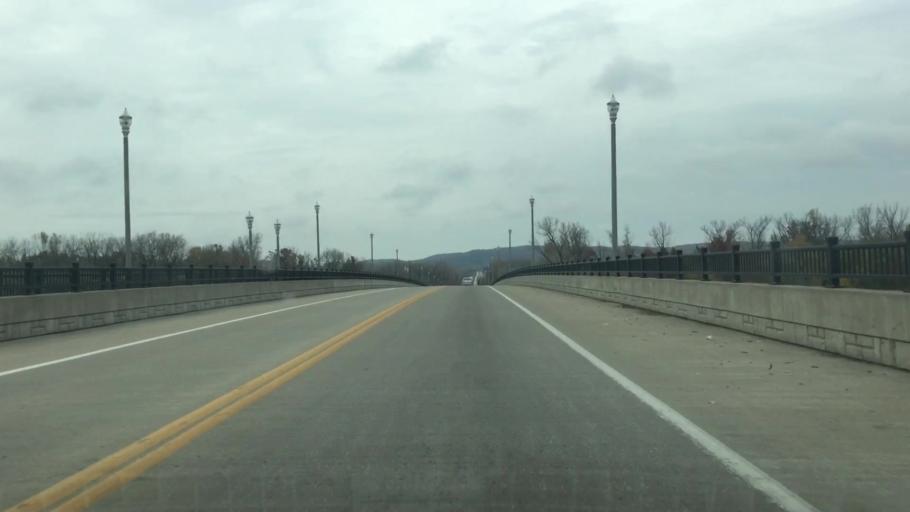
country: US
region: Missouri
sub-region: Gasconade County
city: Hermann
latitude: 38.7093
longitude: -91.4385
